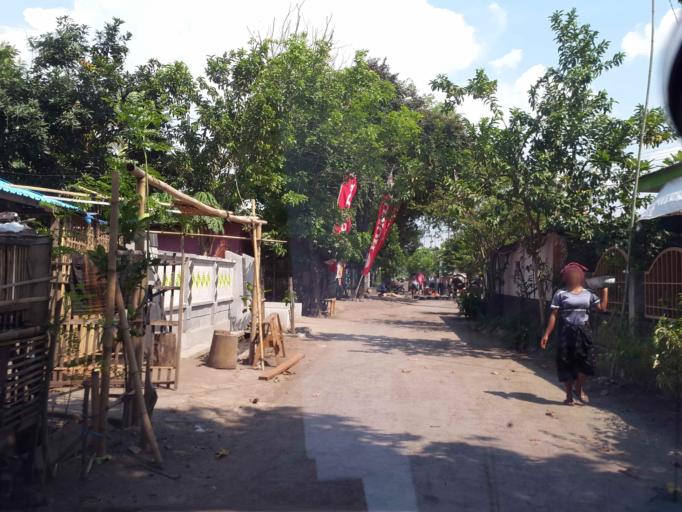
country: ID
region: West Nusa Tenggara
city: Jelateng Timur
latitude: -8.6850
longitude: 116.0955
